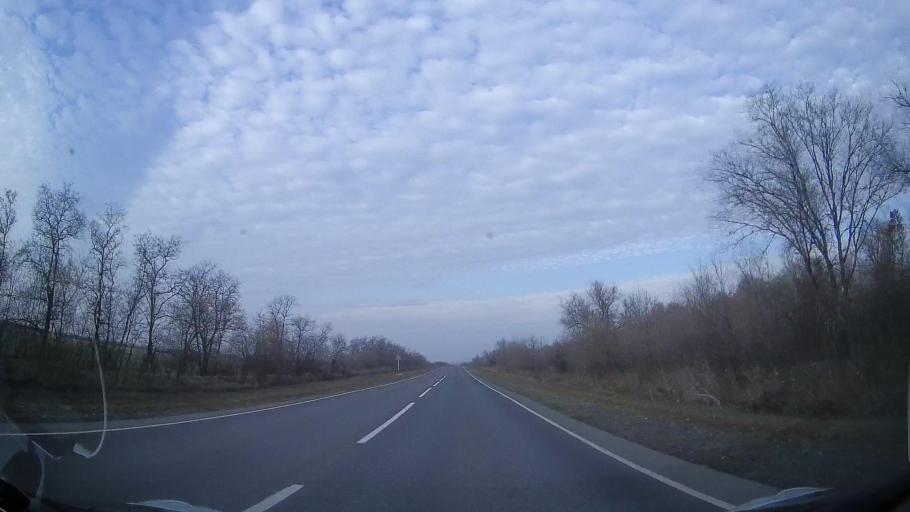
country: RU
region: Rostov
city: Bagayevskaya
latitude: 47.1457
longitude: 40.2766
